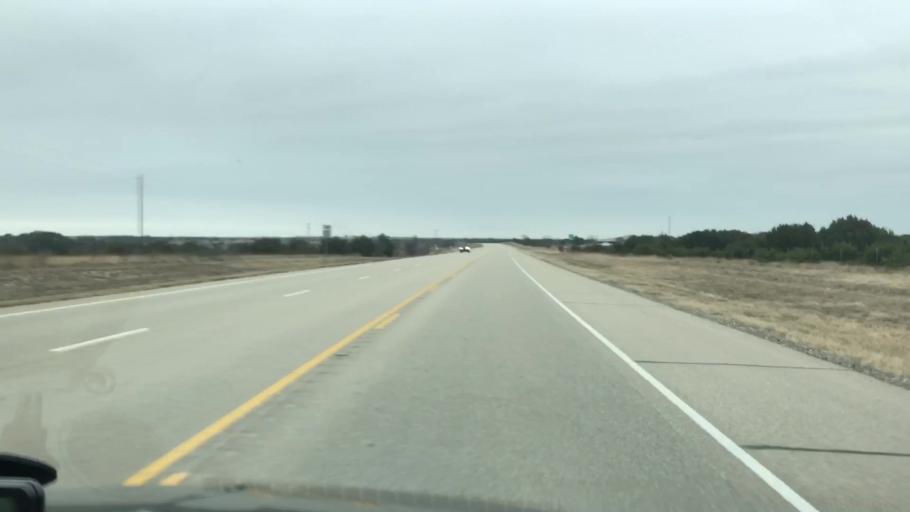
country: US
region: Texas
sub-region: Hamilton County
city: Hamilton
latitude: 31.8458
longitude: -98.1136
